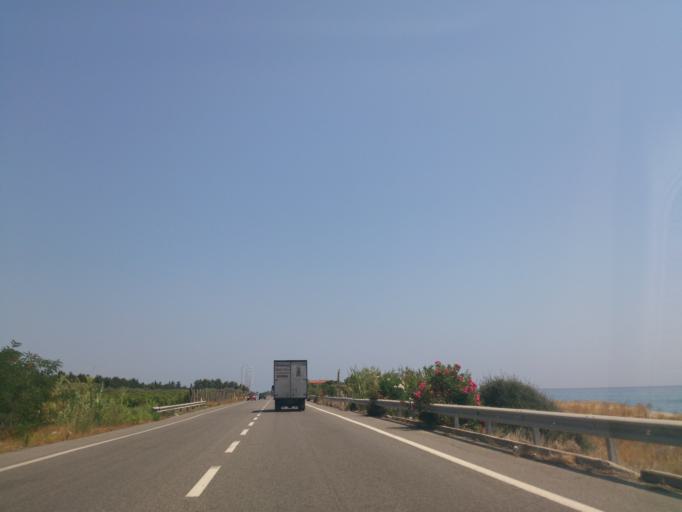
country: IT
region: Calabria
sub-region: Provincia di Reggio Calabria
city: Monasterace Marina
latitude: 38.4127
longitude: 16.5559
